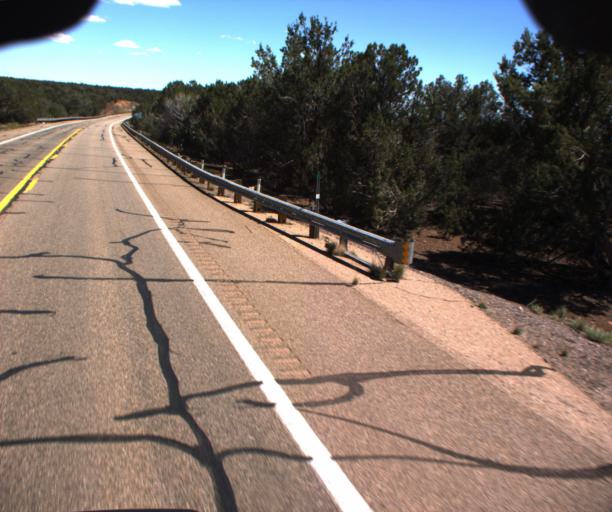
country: US
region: Arizona
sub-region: Yavapai County
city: Paulden
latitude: 35.0867
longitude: -112.4098
